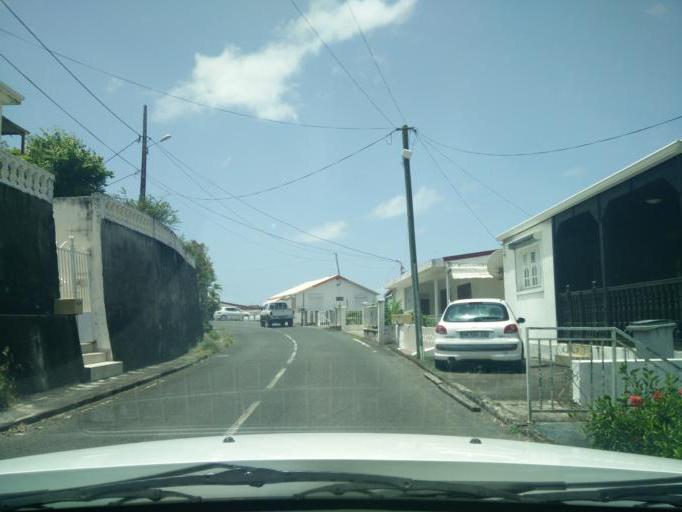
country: GP
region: Guadeloupe
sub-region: Guadeloupe
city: Gourbeyre
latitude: 15.9496
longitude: -61.6950
